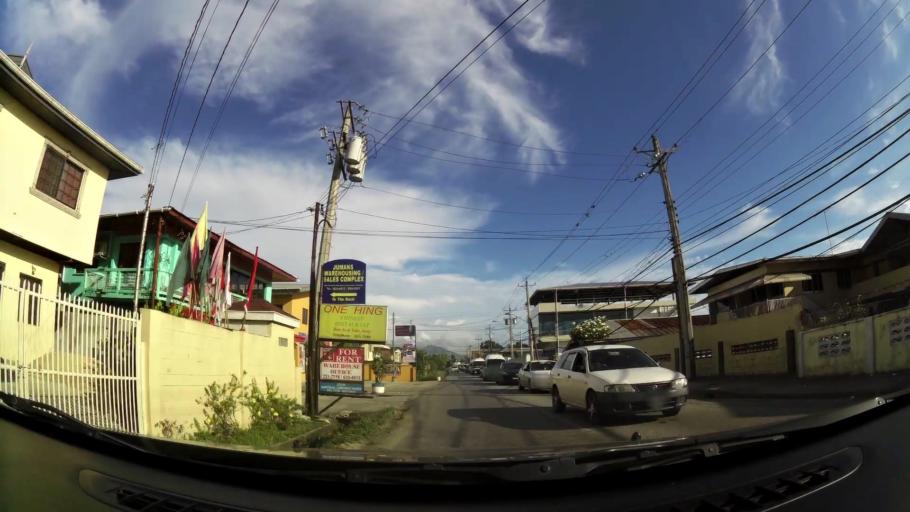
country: TT
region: Tunapuna/Piarco
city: Tunapuna
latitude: 10.5676
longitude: -61.3732
